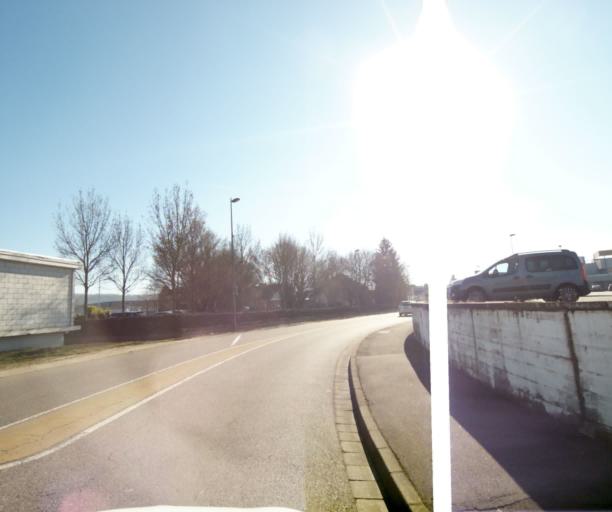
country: FR
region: Lorraine
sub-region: Departement de Meurthe-et-Moselle
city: Maxeville
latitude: 48.7108
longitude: 6.1736
